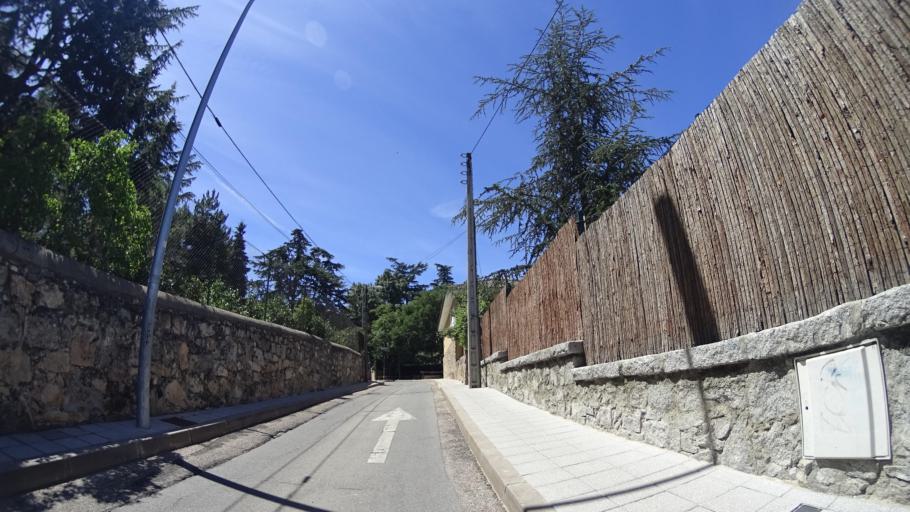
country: ES
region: Madrid
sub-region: Provincia de Madrid
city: Collado-Villalba
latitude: 40.6406
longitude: -3.9911
